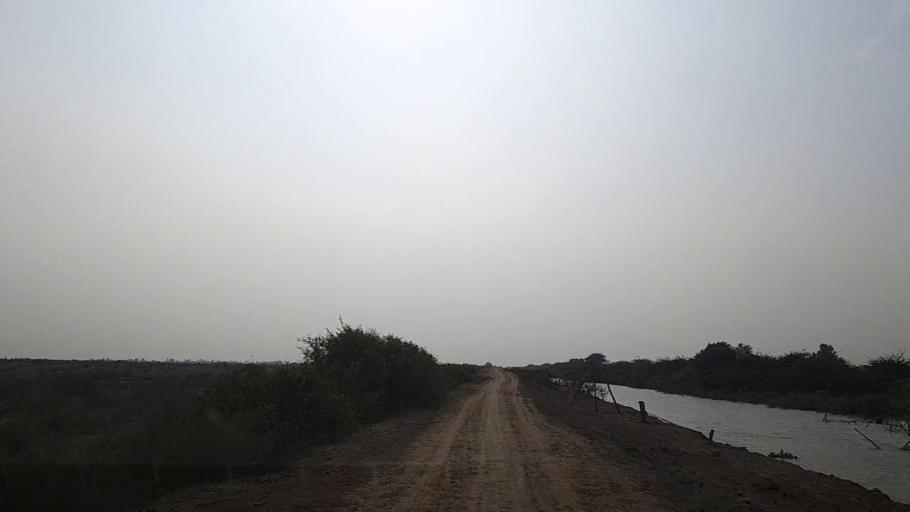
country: PK
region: Sindh
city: Gharo
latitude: 24.6646
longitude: 67.6320
